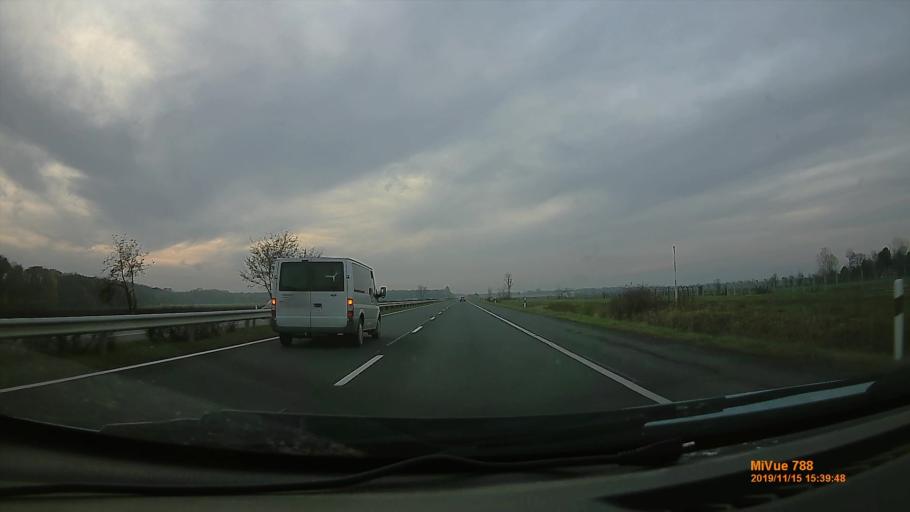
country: HU
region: Bekes
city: Bekescsaba
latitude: 46.6736
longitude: 21.1647
